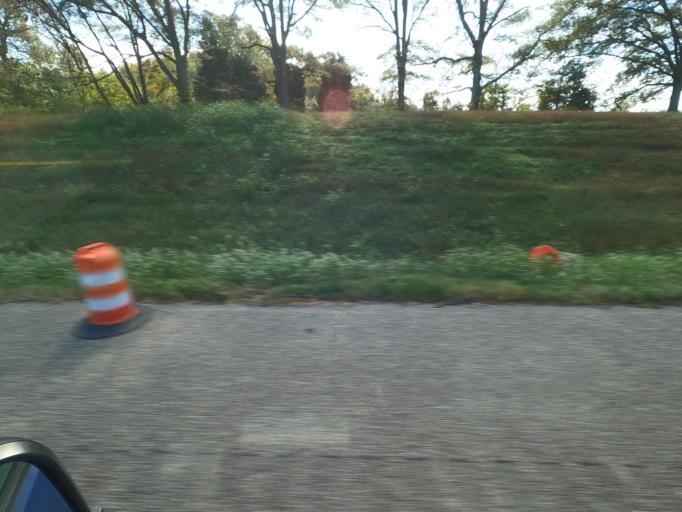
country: US
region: Tennessee
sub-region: Crockett County
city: Bells
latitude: 35.5814
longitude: -89.1057
